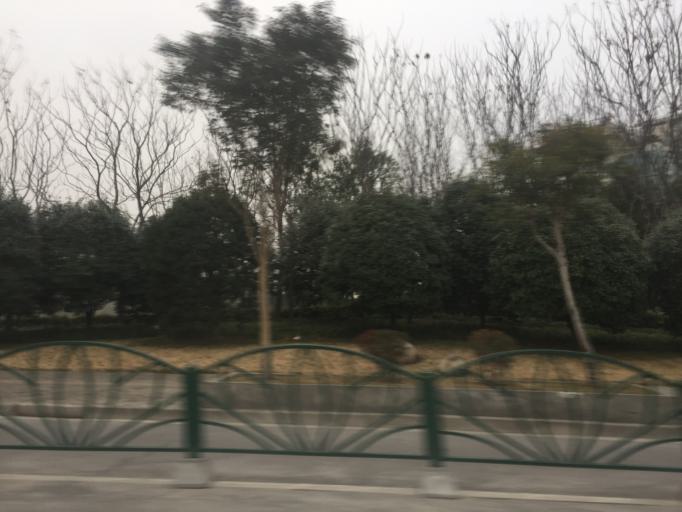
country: CN
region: Shanghai Shi
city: Luwan
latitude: 31.1877
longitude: 121.4968
